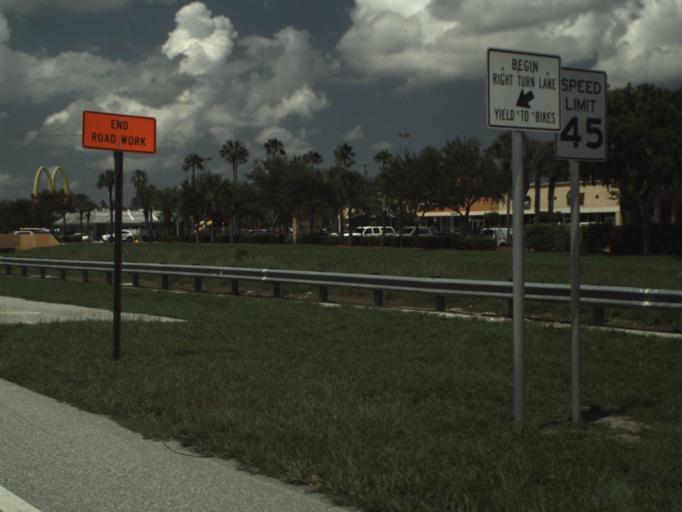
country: US
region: Florida
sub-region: Palm Beach County
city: Boca Pointe
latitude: 26.3686
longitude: -80.2034
